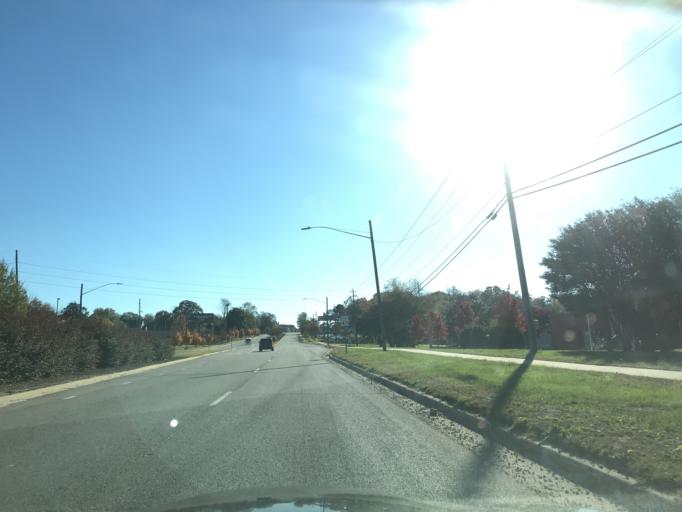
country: US
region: North Carolina
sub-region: Wake County
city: Raleigh
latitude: 35.7534
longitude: -78.6419
